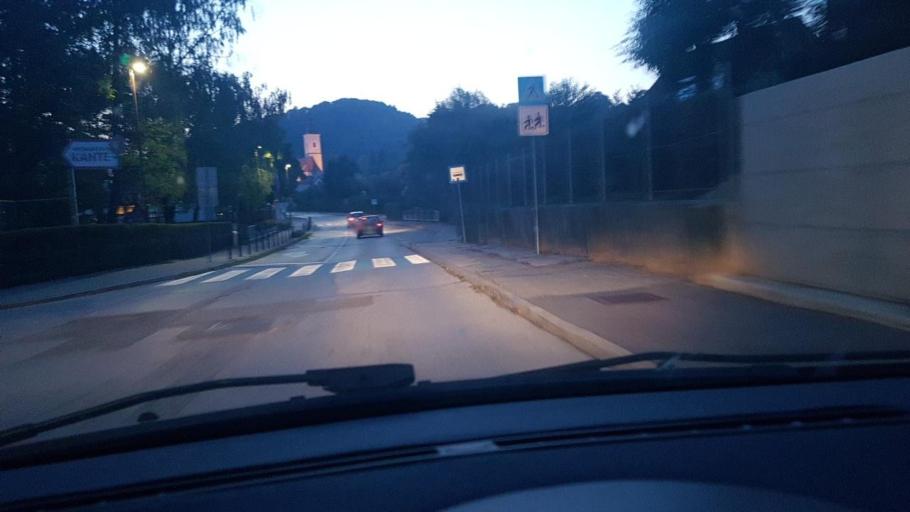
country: SI
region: Maribor
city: Kamnica
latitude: 46.5735
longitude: 15.6166
